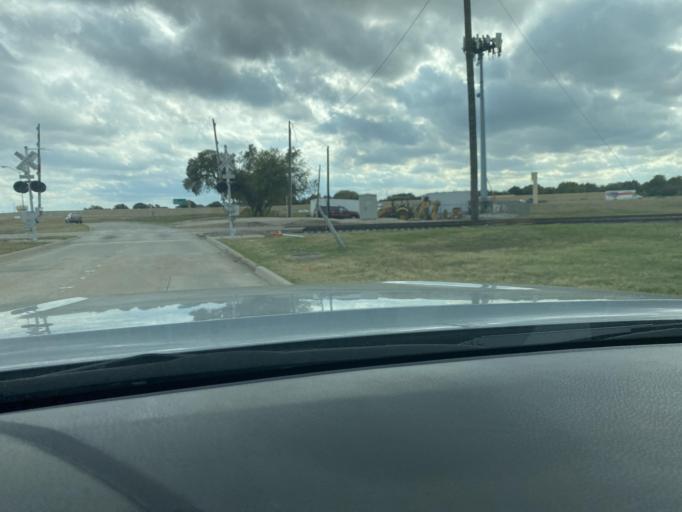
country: US
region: Texas
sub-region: Dallas County
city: Addison
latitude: 33.0122
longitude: -96.7867
